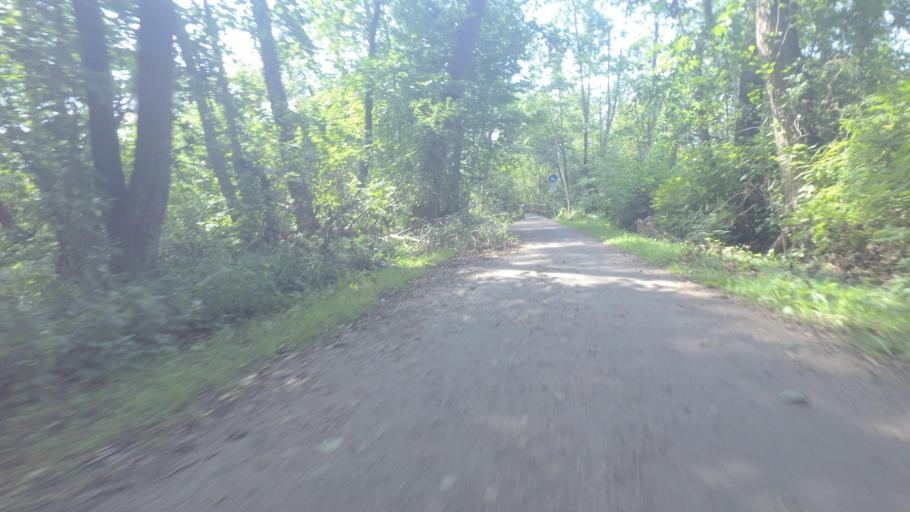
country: DE
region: Mecklenburg-Vorpommern
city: Waren
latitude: 53.5181
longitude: 12.6611
